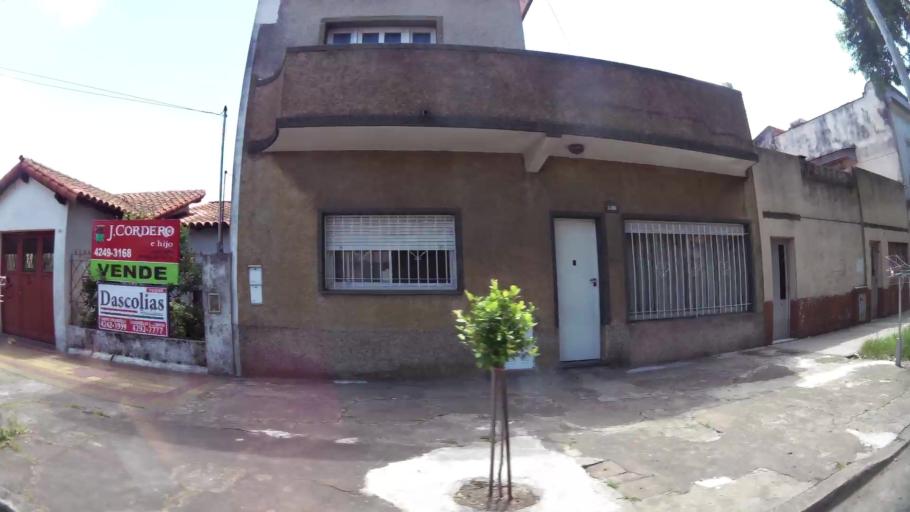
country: AR
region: Buenos Aires
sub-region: Partido de Lomas de Zamora
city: Lomas de Zamora
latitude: -34.7330
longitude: -58.4135
